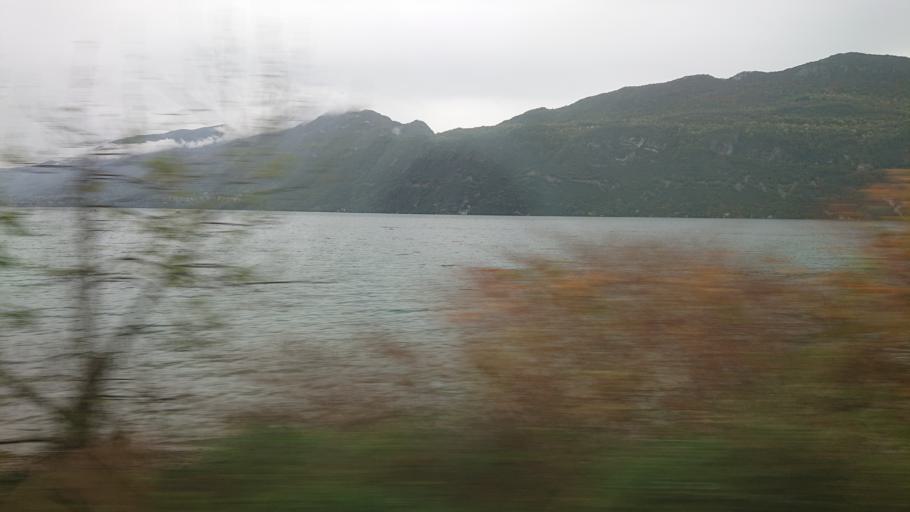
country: FR
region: Rhone-Alpes
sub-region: Departement de la Savoie
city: Brison-Saint-Innocent
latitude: 45.7155
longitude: 5.8877
